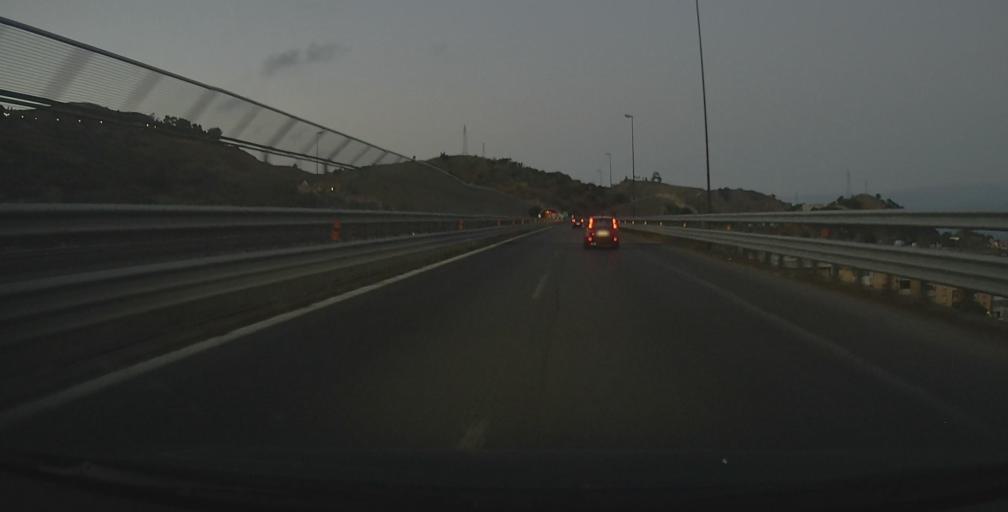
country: IT
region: Sicily
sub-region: Messina
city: Larderia
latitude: 38.1746
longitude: 15.5195
